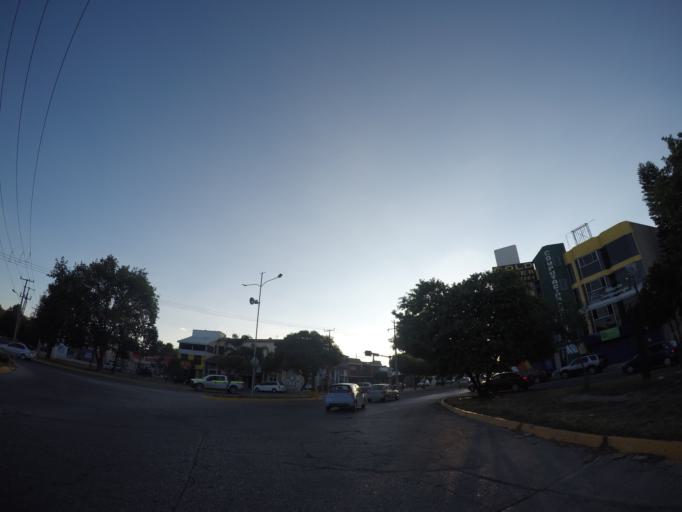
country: MX
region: San Luis Potosi
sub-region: San Luis Potosi
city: San Luis Potosi
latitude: 22.1406
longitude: -100.9935
